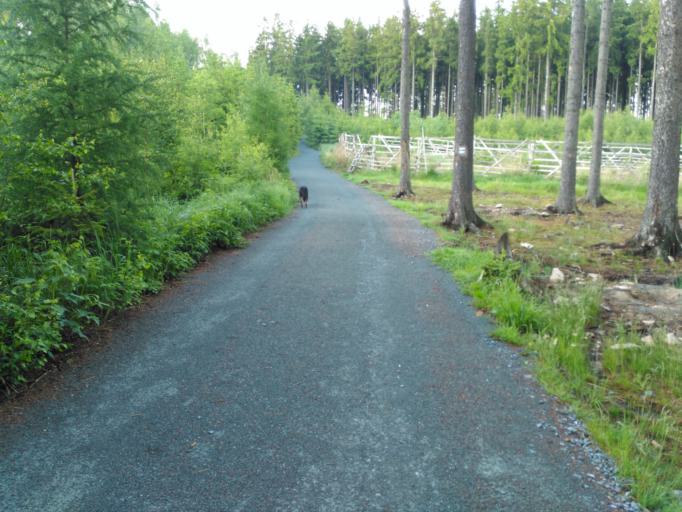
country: CZ
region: Central Bohemia
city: Hudlice
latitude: 49.9629
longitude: 13.9325
